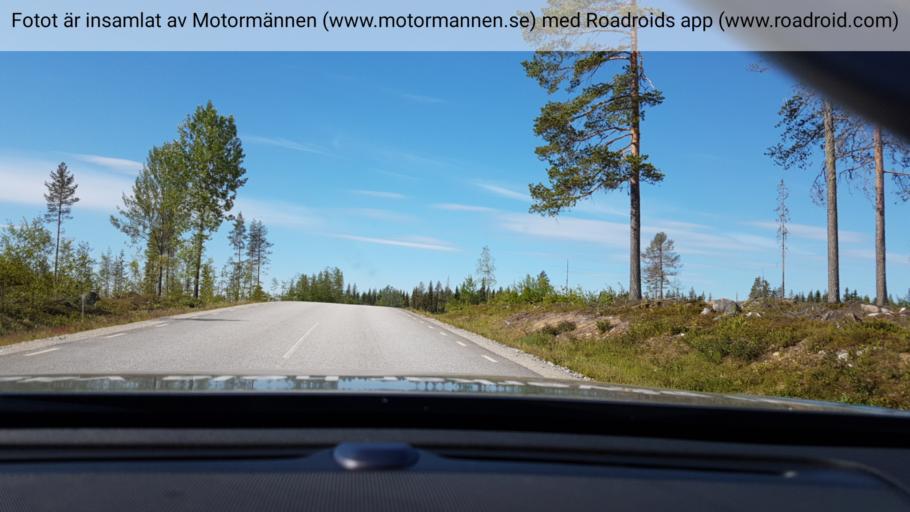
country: SE
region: Vaesterbotten
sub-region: Bjurholms Kommun
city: Bjurholm
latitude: 64.1680
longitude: 19.3893
